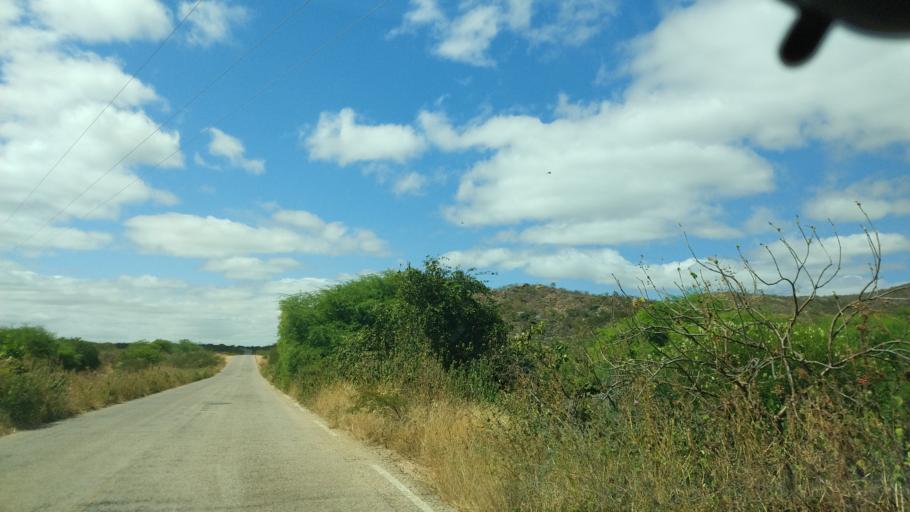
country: BR
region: Rio Grande do Norte
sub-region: Currais Novos
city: Currais Novos
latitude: -6.2653
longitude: -36.5637
